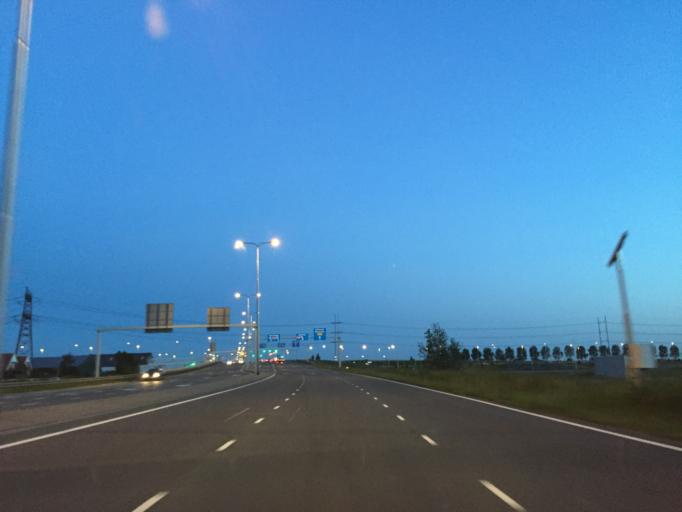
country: NL
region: South Holland
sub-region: Gemeente Lansingerland
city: Bleiswijk
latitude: 52.0408
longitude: 4.5423
